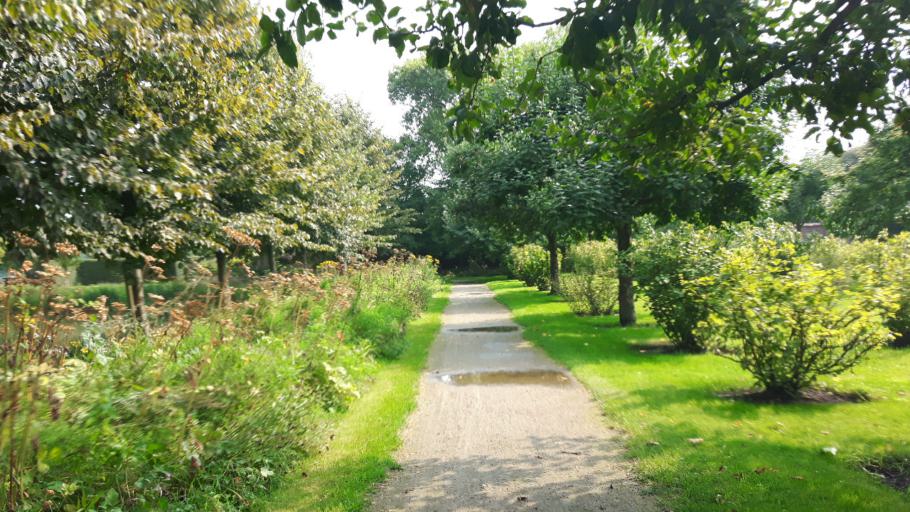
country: NL
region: Groningen
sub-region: Gemeente Bedum
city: Bedum
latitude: 53.3534
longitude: 6.6456
